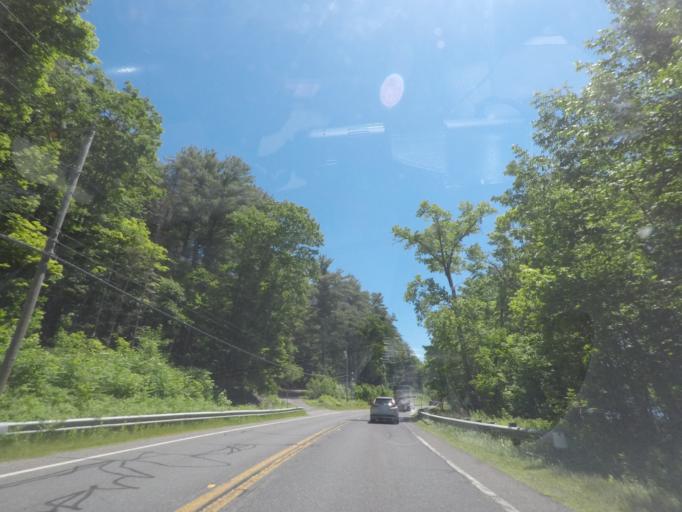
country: US
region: Massachusetts
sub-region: Berkshire County
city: Becket
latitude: 42.2899
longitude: -73.1547
